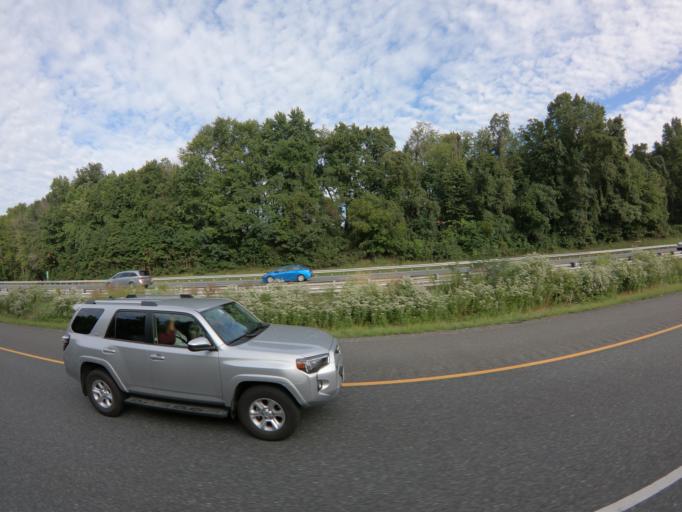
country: US
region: Maryland
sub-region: Harford County
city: Aberdeen
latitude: 39.5396
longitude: -76.1814
